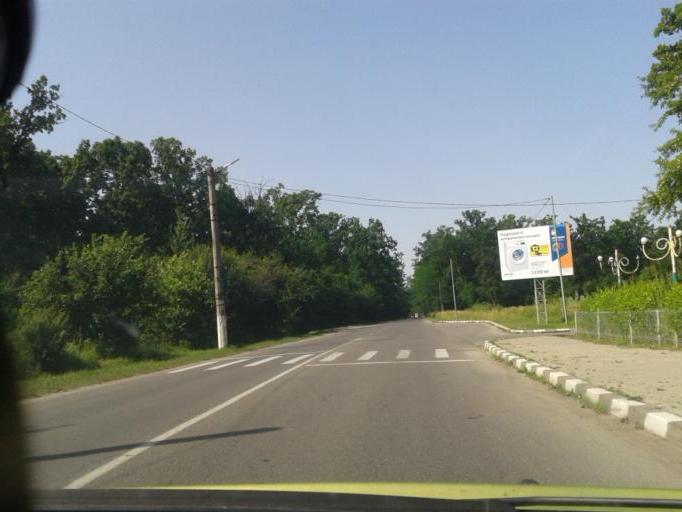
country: RO
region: Prahova
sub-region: Comuna Paulesti
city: Gageni
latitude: 45.0469
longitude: 25.9493
